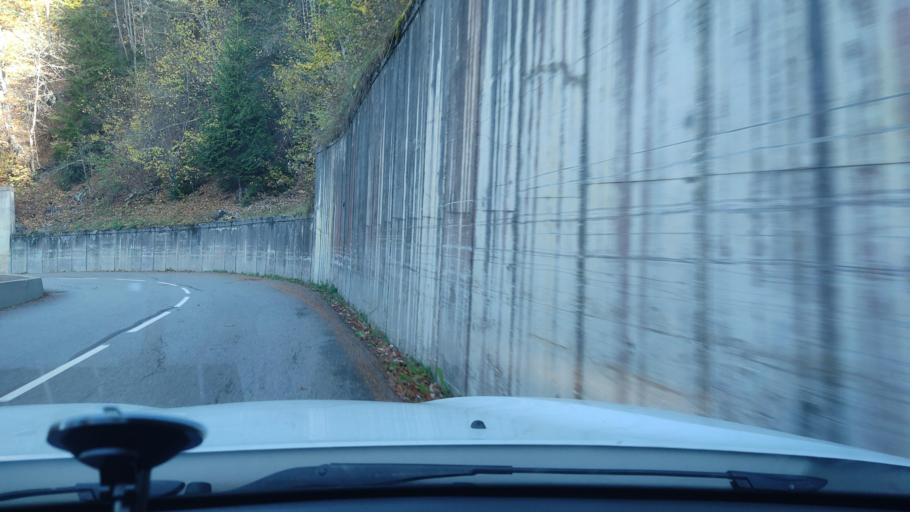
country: FR
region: Rhone-Alpes
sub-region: Departement de la Savoie
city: Villargondran
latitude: 45.2249
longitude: 6.3351
